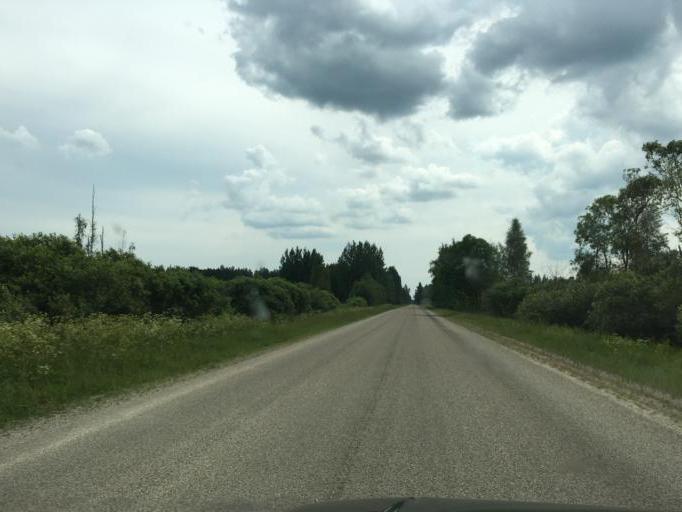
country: LV
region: Rugaju
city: Rugaji
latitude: 56.8340
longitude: 27.0936
